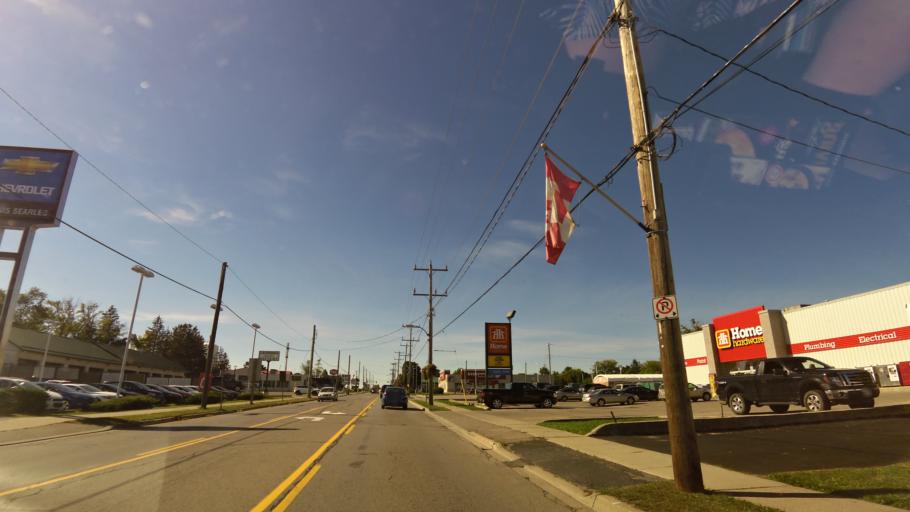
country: CA
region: Ontario
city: Ancaster
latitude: 43.0675
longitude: -79.9564
